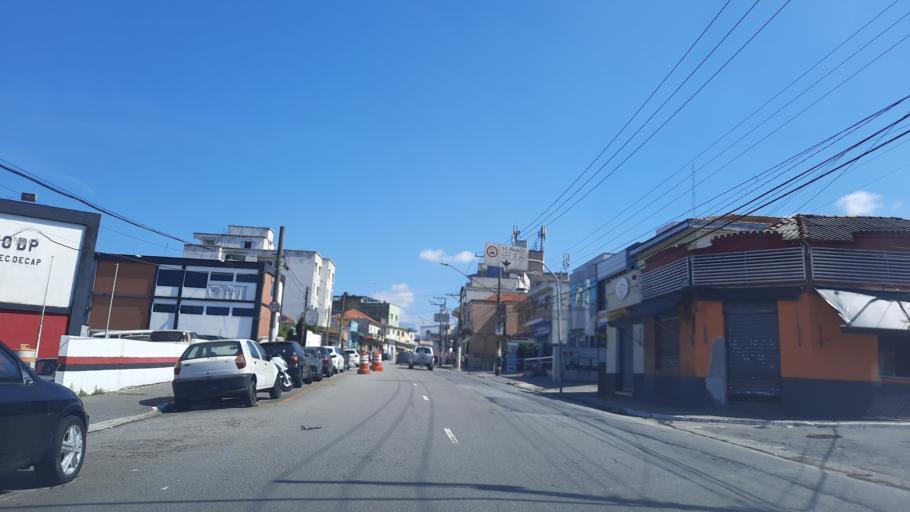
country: BR
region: Sao Paulo
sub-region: Sao Paulo
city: Sao Paulo
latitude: -23.4945
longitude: -46.6776
